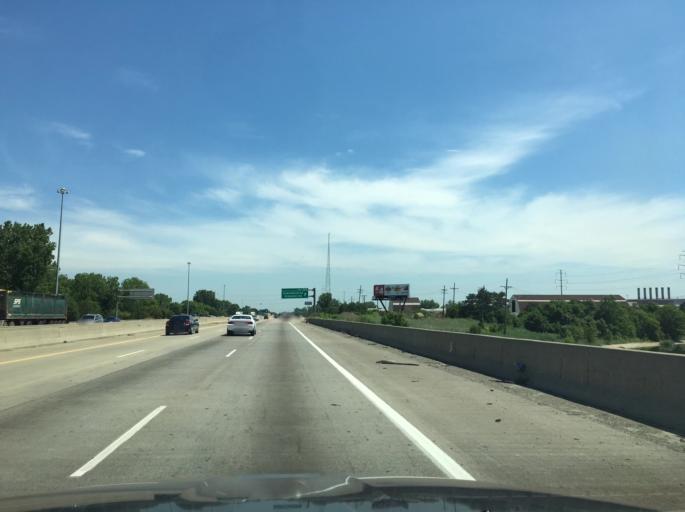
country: US
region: Michigan
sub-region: Wayne County
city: Melvindale
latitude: 42.2948
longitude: -83.1877
